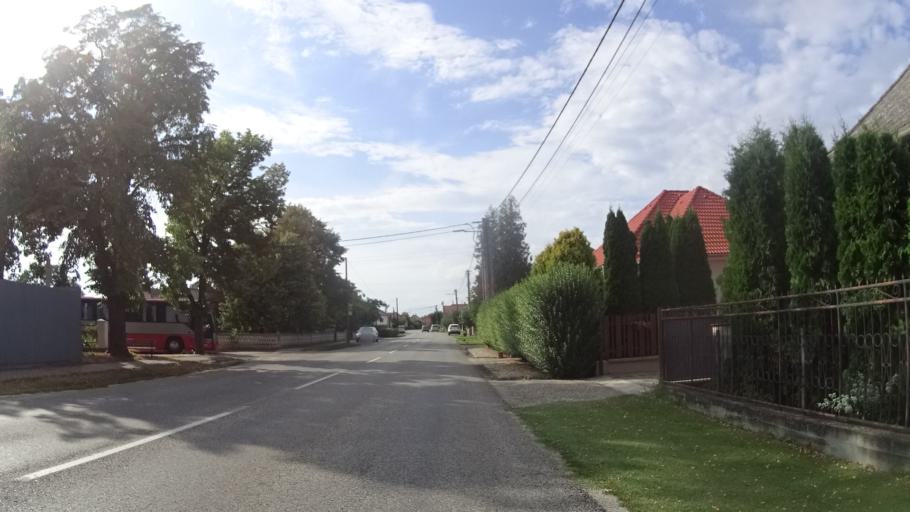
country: SK
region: Trnavsky
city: Gabcikovo
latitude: 47.9181
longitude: 17.5025
